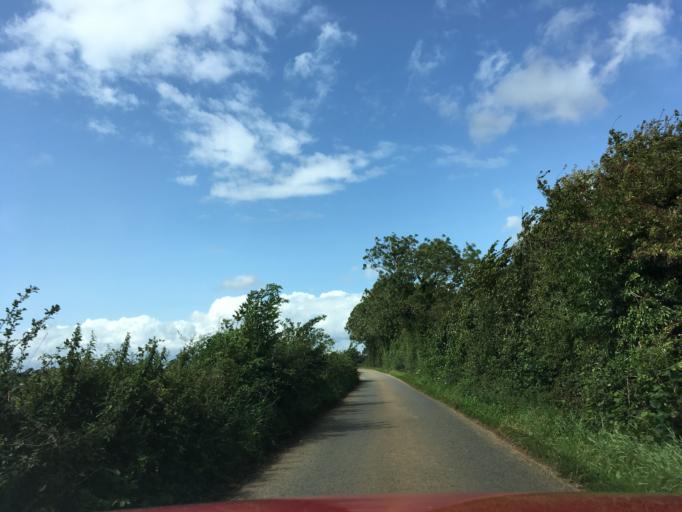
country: GB
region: England
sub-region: Wiltshire
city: Luckington
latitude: 51.5950
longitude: -2.2363
